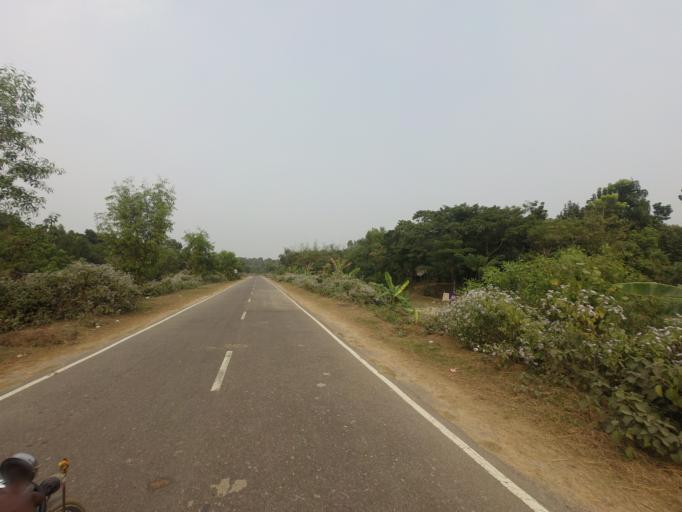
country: BD
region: Dhaka
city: Netrakona
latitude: 25.1656
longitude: 90.6585
